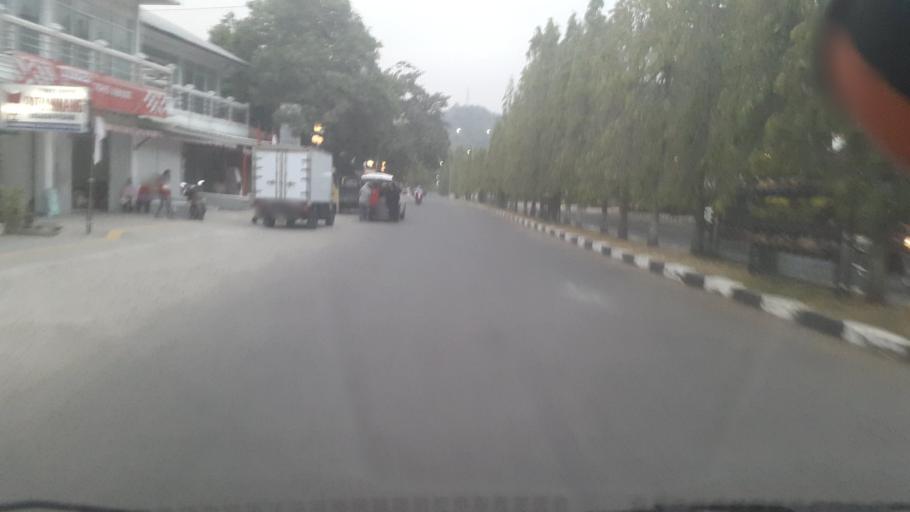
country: ID
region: West Java
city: Pelabuhanratu
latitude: -6.9869
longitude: 106.5571
